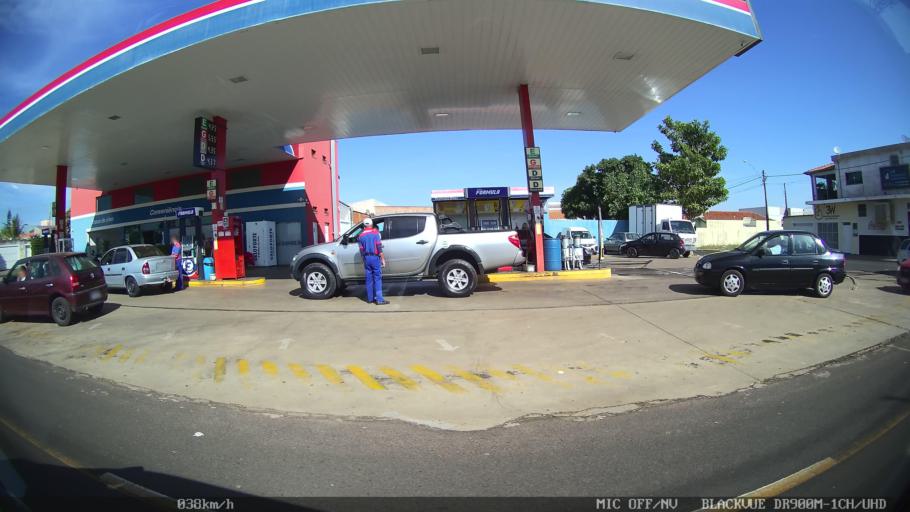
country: BR
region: Sao Paulo
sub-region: Franca
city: Franca
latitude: -20.5083
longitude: -47.4246
